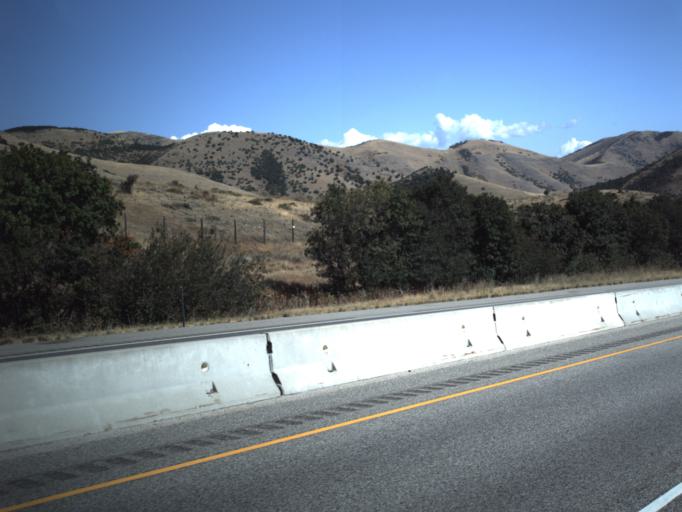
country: US
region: Utah
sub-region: Box Elder County
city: Brigham City
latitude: 41.5313
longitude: -111.9562
